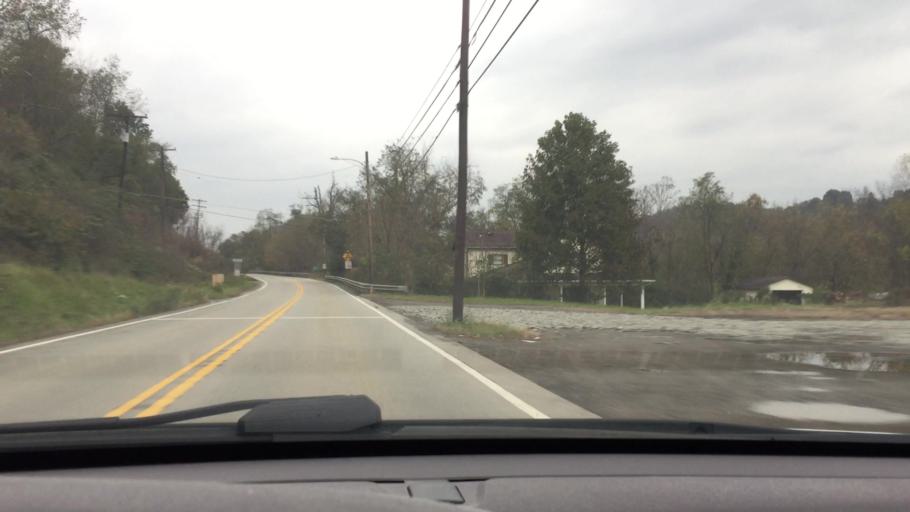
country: US
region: Pennsylvania
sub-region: Fayette County
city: Fairhope
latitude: 40.1102
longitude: -79.8520
